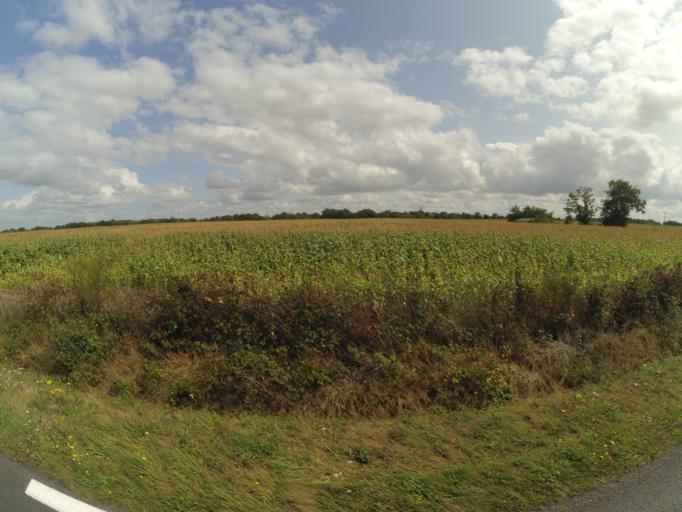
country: FR
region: Pays de la Loire
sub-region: Departement de la Vendee
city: La Bernardiere
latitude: 47.0175
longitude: -1.2741
